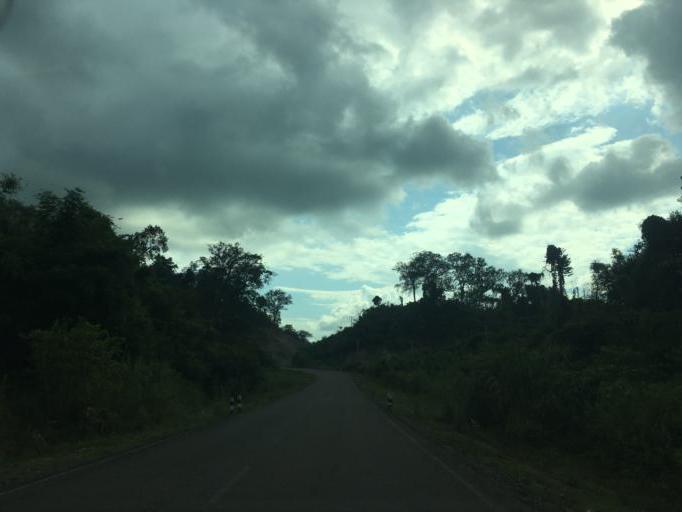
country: TH
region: Nong Khai
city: Sangkhom
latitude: 18.1965
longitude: 102.2224
